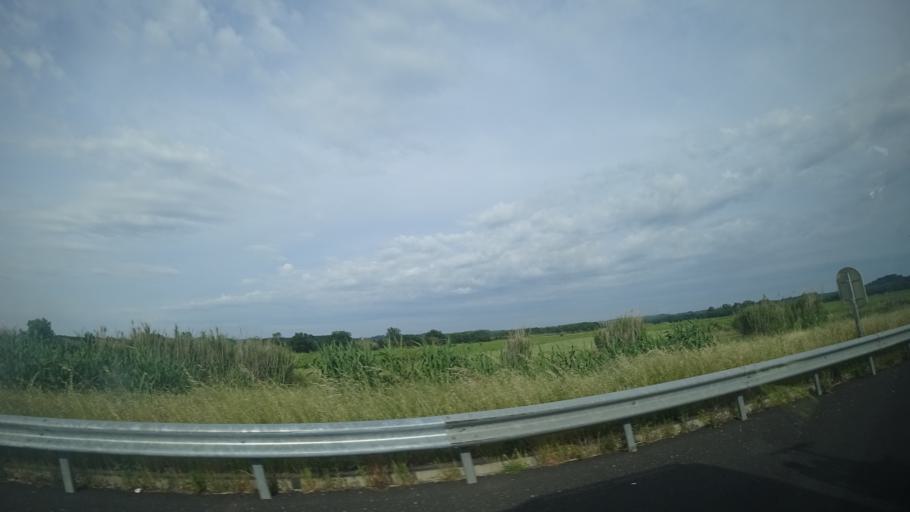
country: FR
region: Languedoc-Roussillon
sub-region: Departement de l'Herault
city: Lezignan-la-Cebe
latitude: 43.4988
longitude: 3.4458
